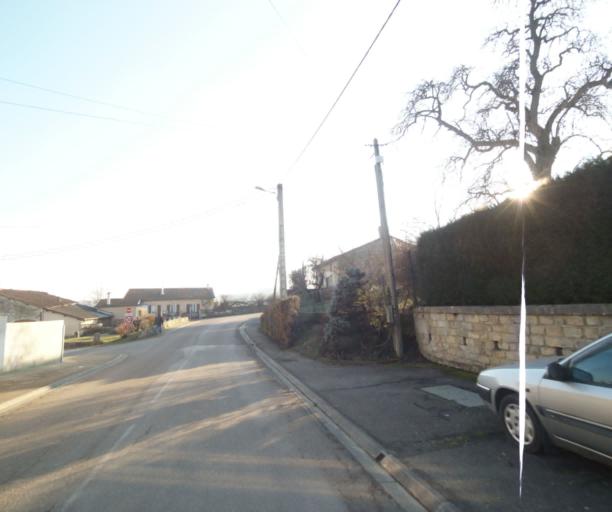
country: FR
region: Champagne-Ardenne
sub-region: Departement de la Haute-Marne
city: Bienville
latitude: 48.5812
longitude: 5.0885
